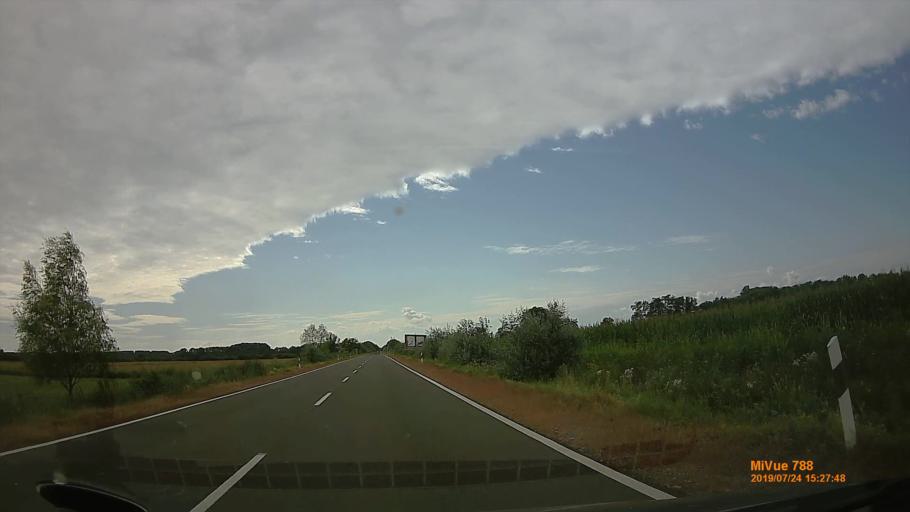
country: HU
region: Szabolcs-Szatmar-Bereg
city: Tarpa
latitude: 48.1608
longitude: 22.4922
